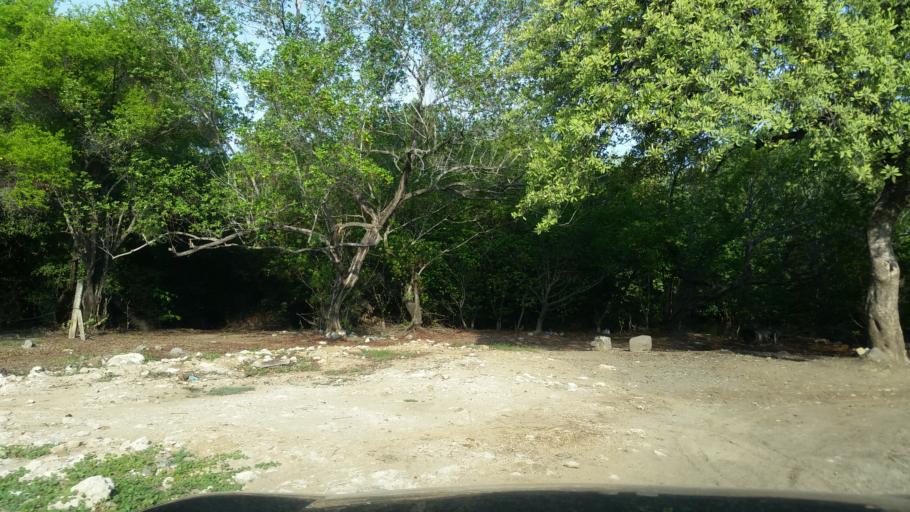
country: NI
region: Managua
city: Masachapa
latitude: 11.7529
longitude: -86.4840
